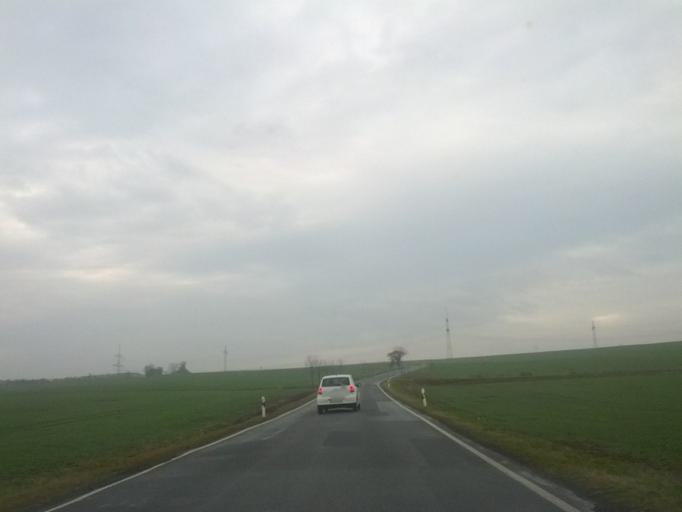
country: DE
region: Thuringia
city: Friedrichswerth
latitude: 50.9847
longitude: 10.5461
